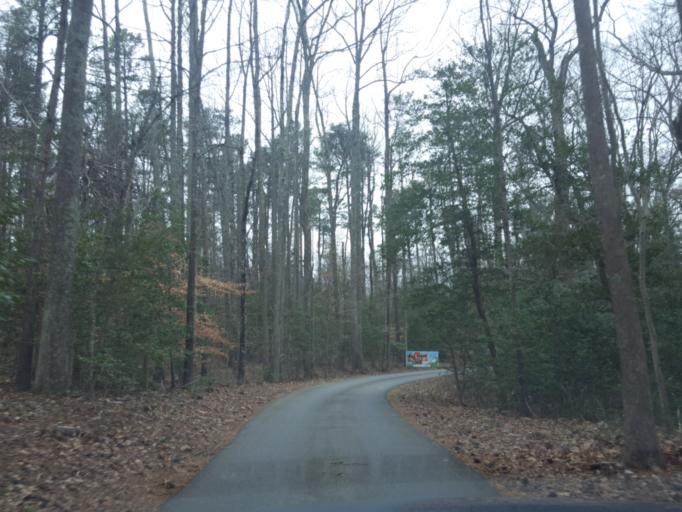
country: US
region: Maryland
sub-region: Calvert County
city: Lusby
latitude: 38.4033
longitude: -76.5026
